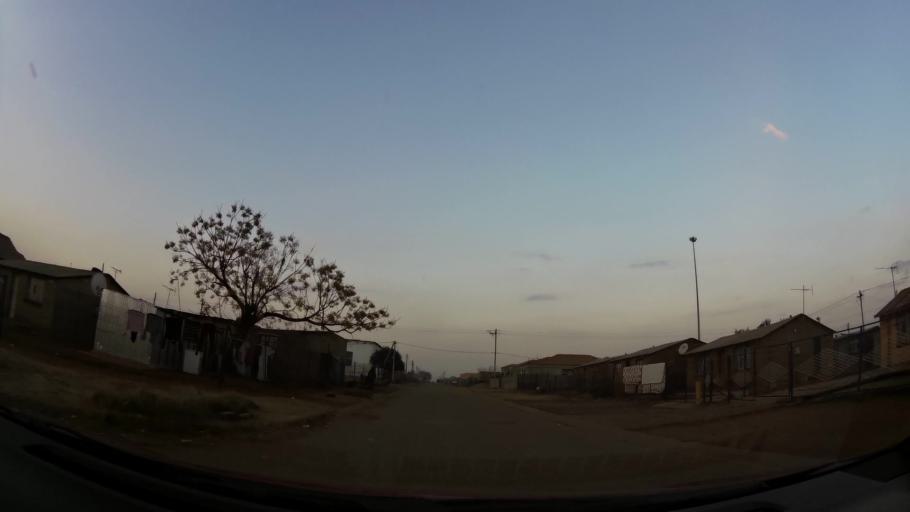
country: ZA
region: Gauteng
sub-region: City of Johannesburg Metropolitan Municipality
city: Orange Farm
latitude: -26.5527
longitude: 27.8740
